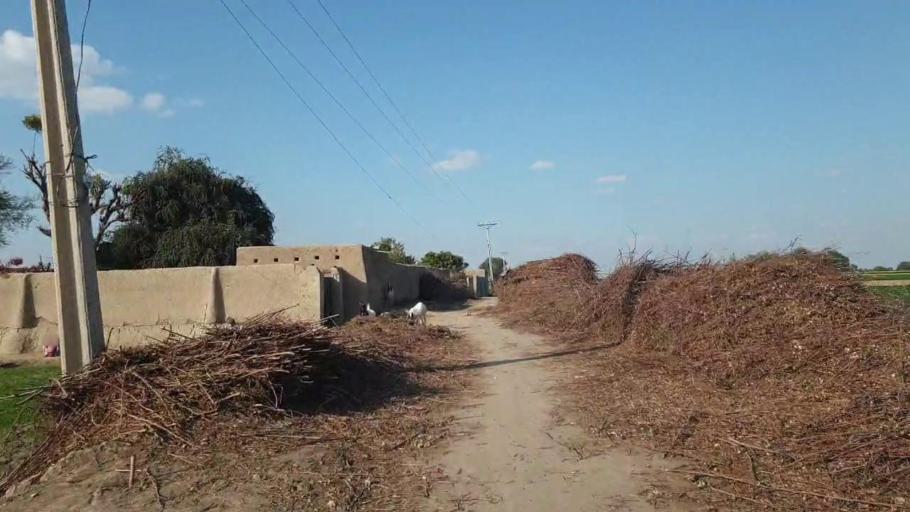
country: PK
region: Sindh
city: Shahpur Chakar
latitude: 26.1064
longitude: 68.5826
